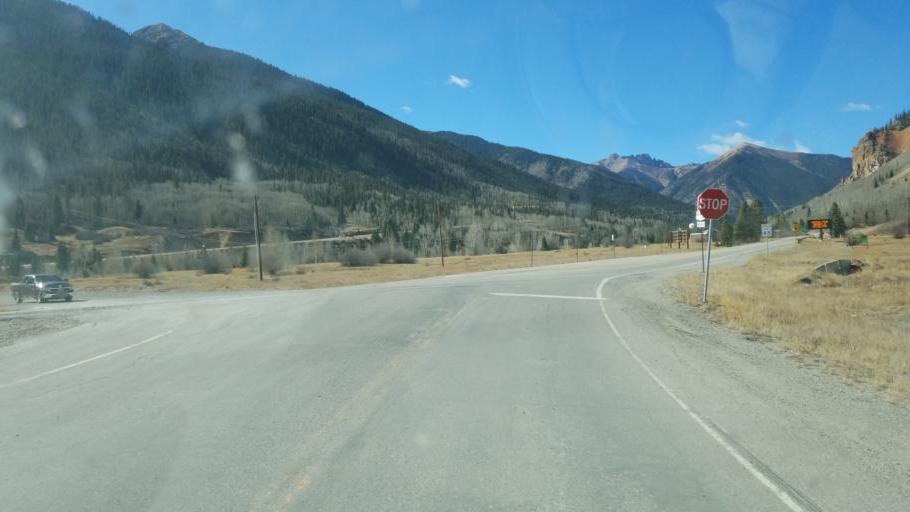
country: US
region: Colorado
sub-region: San Juan County
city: Silverton
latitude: 37.8054
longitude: -107.6717
